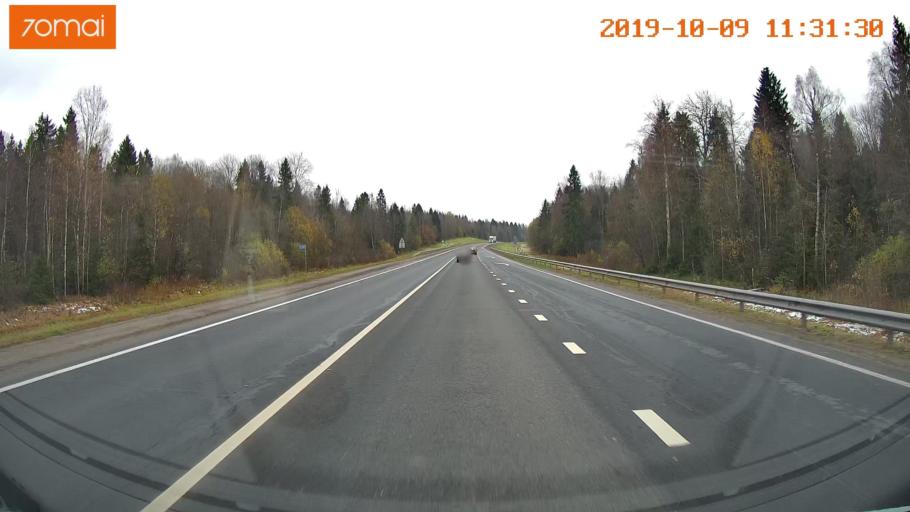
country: RU
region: Vologda
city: Gryazovets
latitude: 59.0449
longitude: 40.0973
